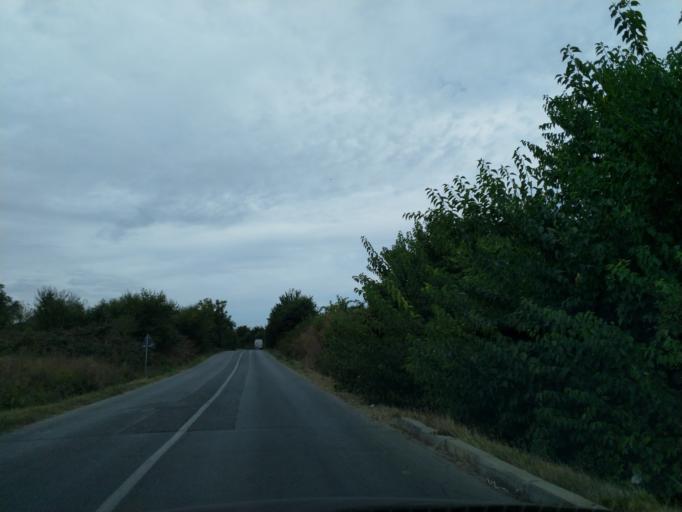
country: RS
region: Central Serbia
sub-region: Pomoravski Okrug
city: Jagodina
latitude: 43.9878
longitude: 21.2365
